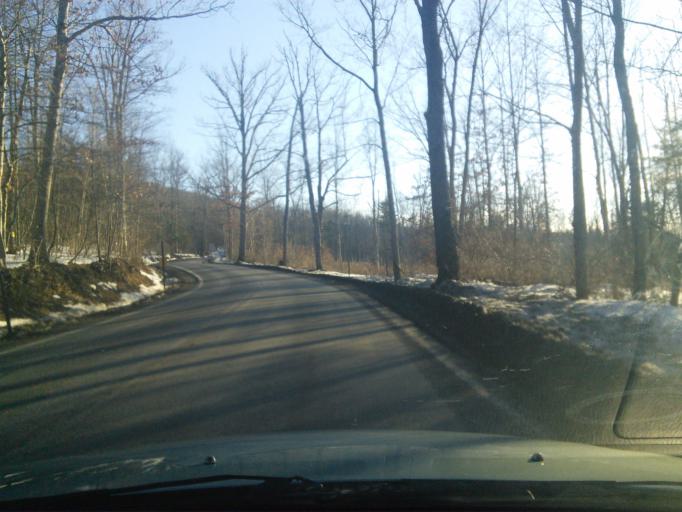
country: US
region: Pennsylvania
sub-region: Centre County
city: Park Forest Village
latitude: 40.8612
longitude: -77.9329
